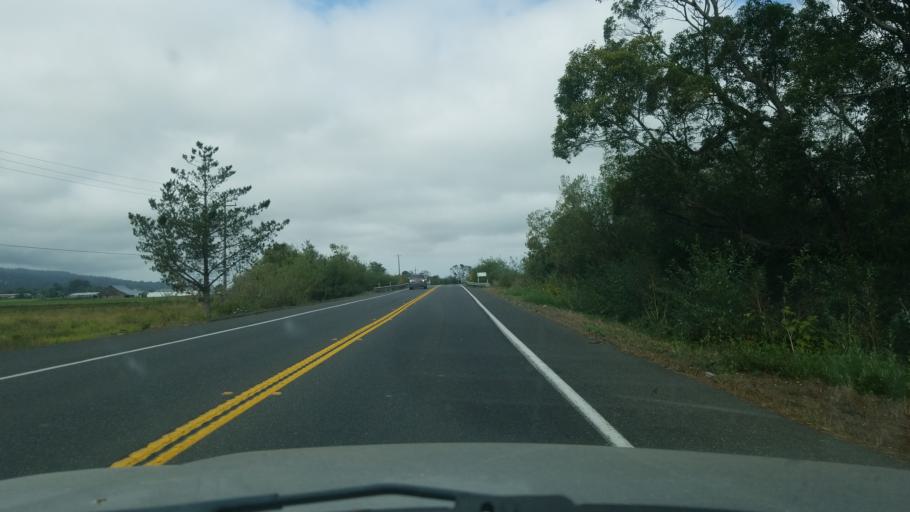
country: US
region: California
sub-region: Humboldt County
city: Ferndale
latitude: 40.5954
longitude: -124.2395
